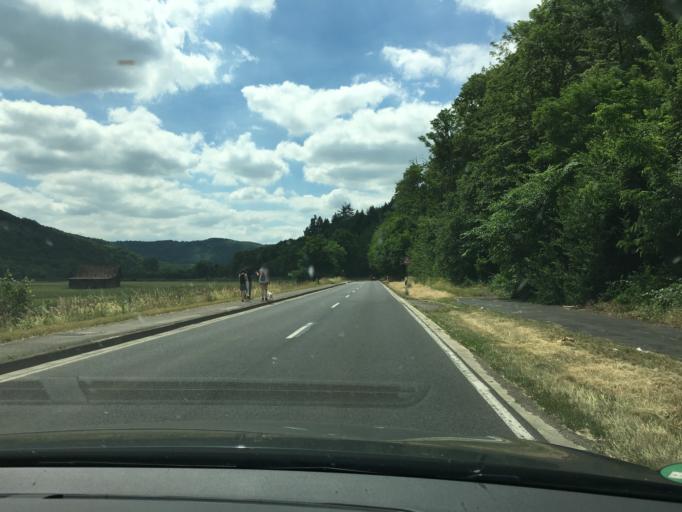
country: DE
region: North Rhine-Westphalia
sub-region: Regierungsbezirk Koln
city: Kreuzau
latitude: 50.7247
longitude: 6.4531
